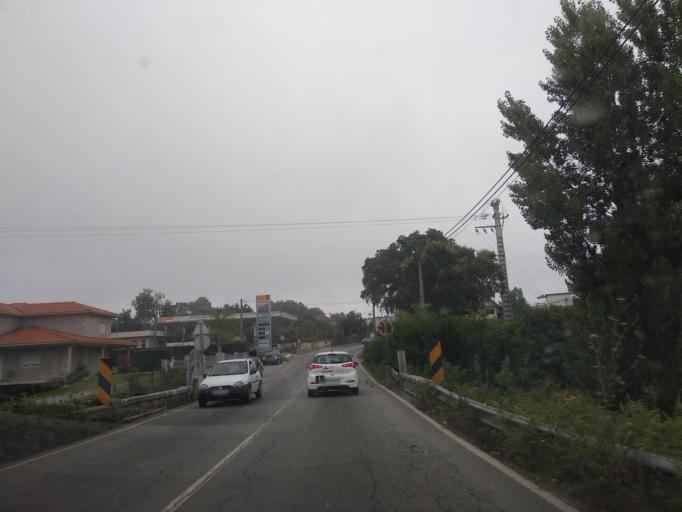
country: PT
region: Braga
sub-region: Vila Verde
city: Vila Verde
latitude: 41.6398
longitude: -8.4349
